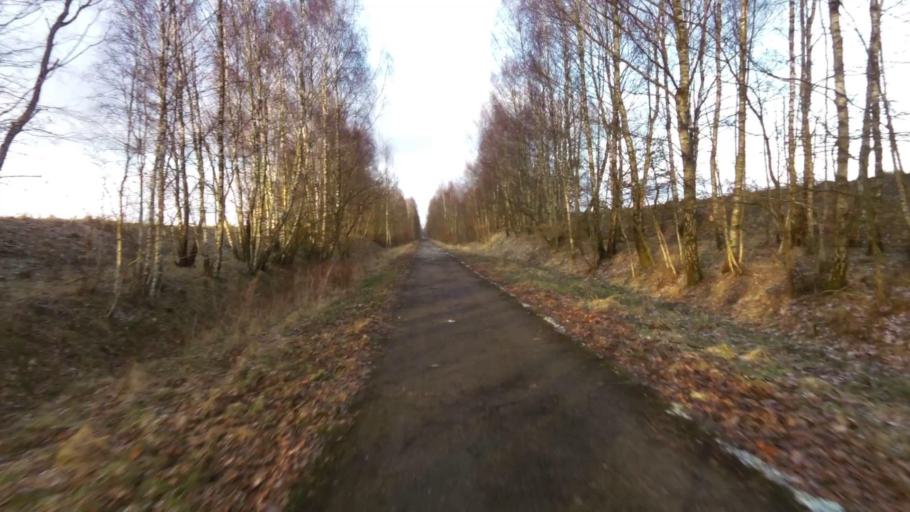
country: PL
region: West Pomeranian Voivodeship
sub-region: Powiat drawski
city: Zlocieniec
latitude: 53.6103
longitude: 16.0501
